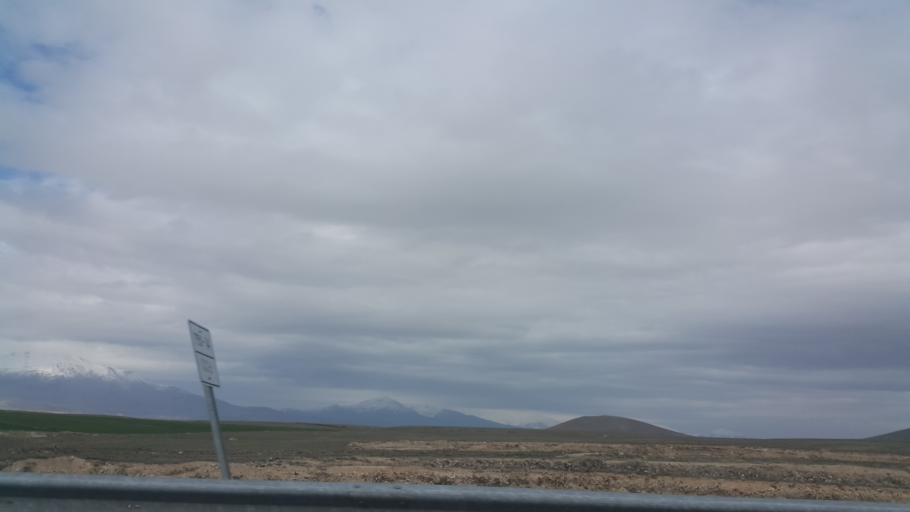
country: TR
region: Aksaray
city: Taspinar
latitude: 37.9764
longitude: 34.0752
